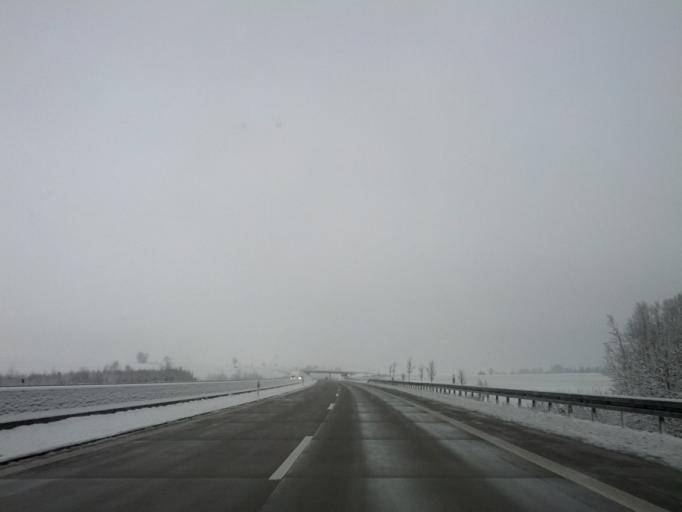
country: DE
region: Bavaria
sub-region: Regierungsbezirk Unterfranken
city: Rodelmaier
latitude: 50.3019
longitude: 10.2786
